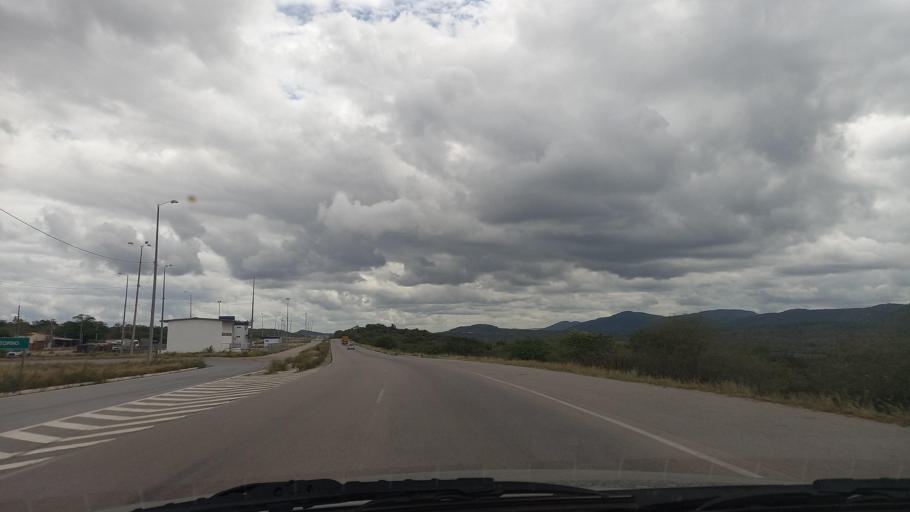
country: BR
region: Pernambuco
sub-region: Caruaru
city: Caruaru
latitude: -8.3205
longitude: -36.0811
